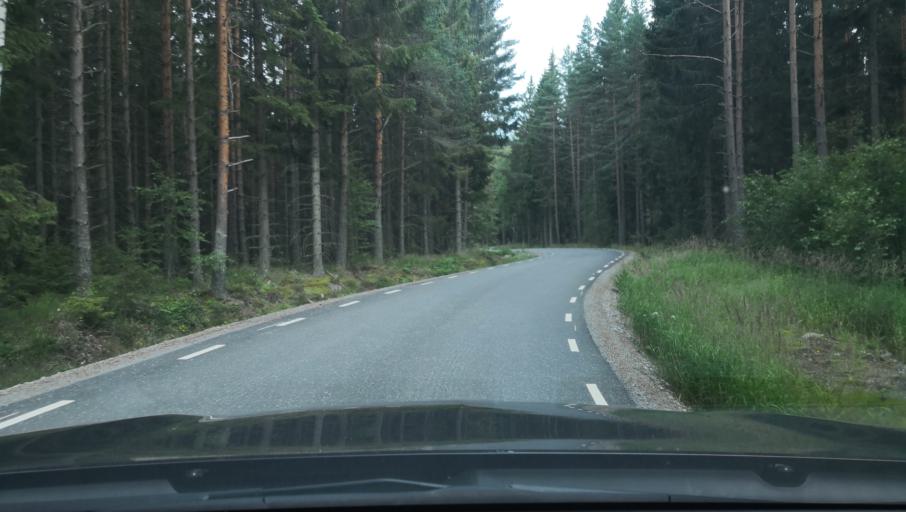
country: SE
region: Vaestmanland
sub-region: Surahammars Kommun
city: Surahammar
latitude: 59.6691
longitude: 16.1372
